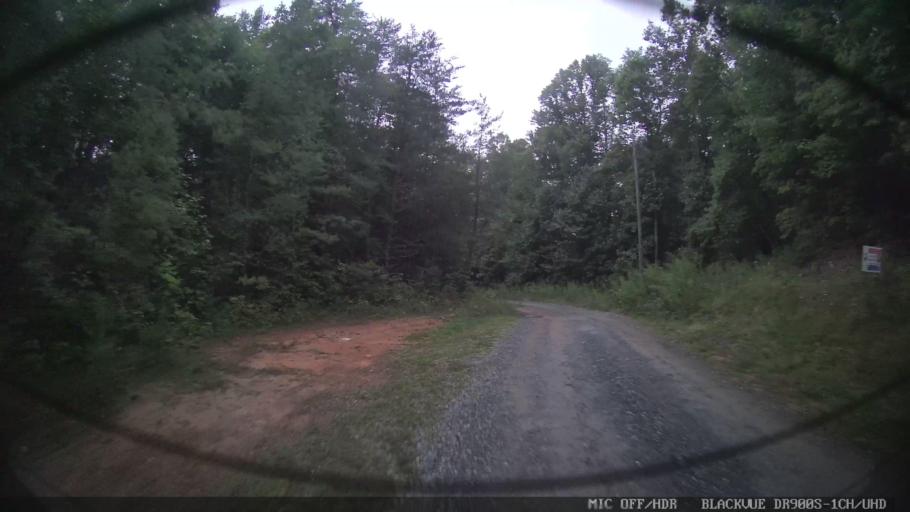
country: US
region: Georgia
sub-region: Gilmer County
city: Ellijay
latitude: 34.7006
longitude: -84.3303
